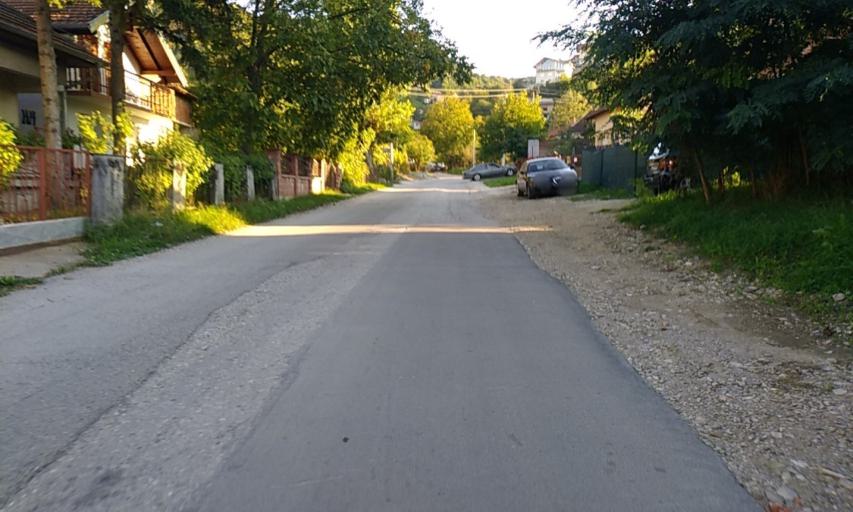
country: BA
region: Republika Srpska
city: Mejdan - Obilicevo
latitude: 44.7568
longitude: 17.1910
